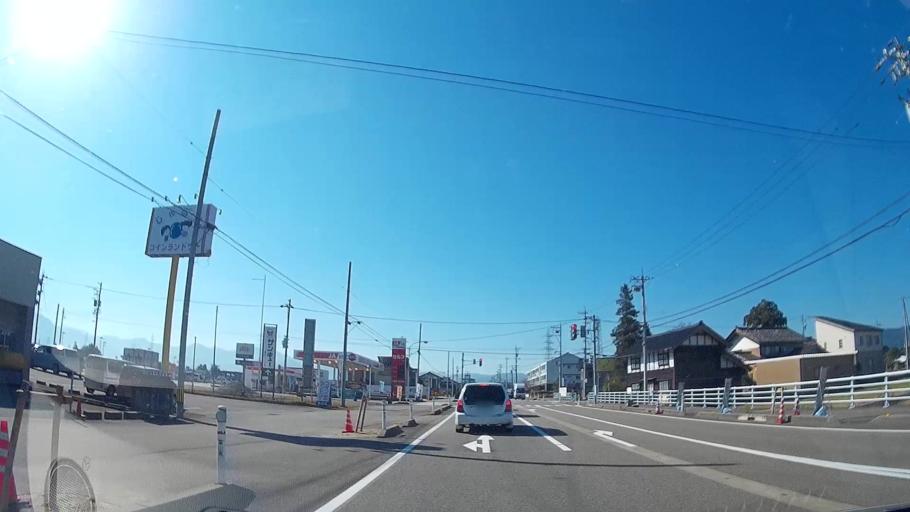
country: JP
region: Toyama
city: Fukumitsu
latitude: 36.5661
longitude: 136.8857
